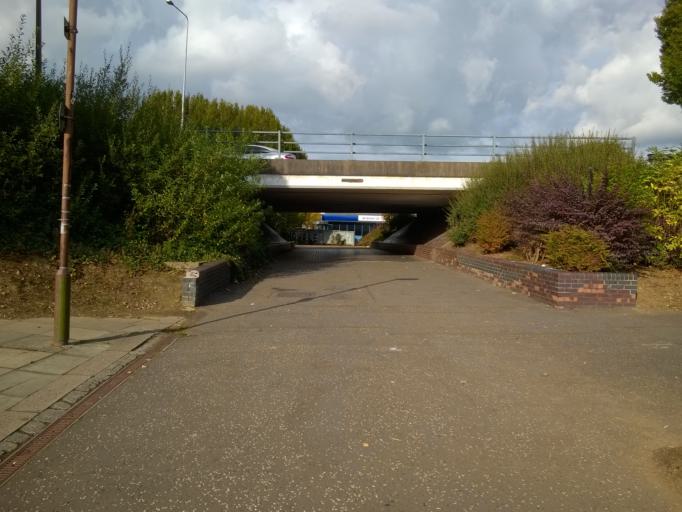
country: GB
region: Scotland
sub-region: West Lothian
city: Livingston
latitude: 55.8830
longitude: -3.5089
